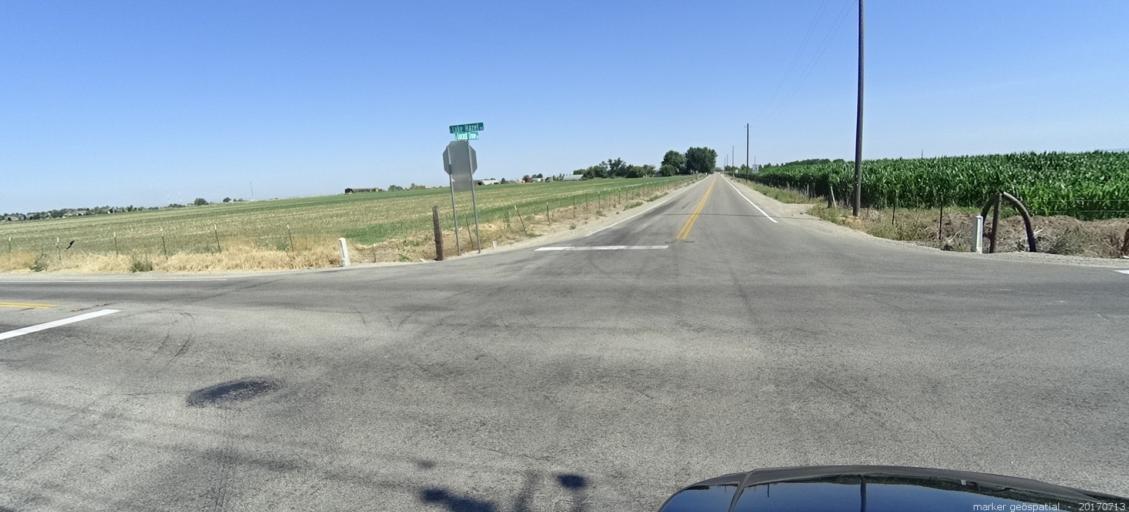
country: US
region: Idaho
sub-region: Ada County
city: Meridian
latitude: 43.5464
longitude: -116.3745
